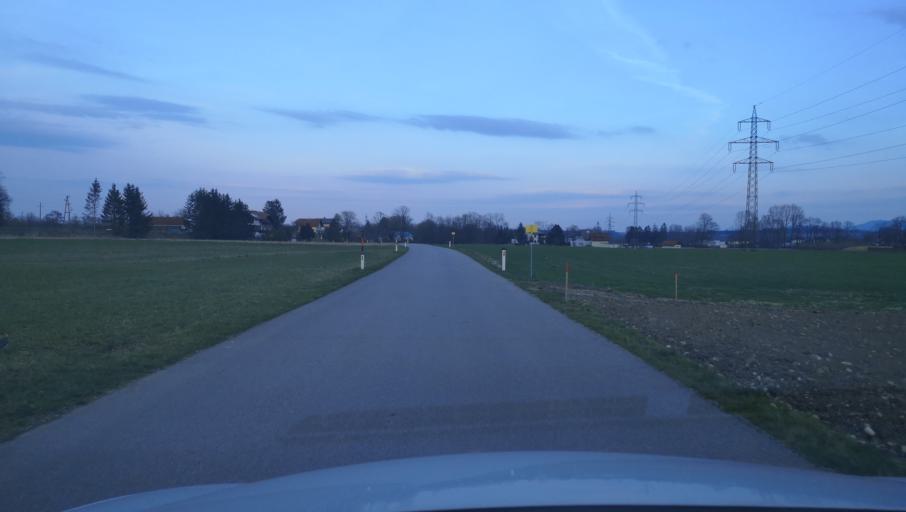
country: AT
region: Lower Austria
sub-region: Politischer Bezirk Amstetten
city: Amstetten
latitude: 48.1051
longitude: 14.8970
